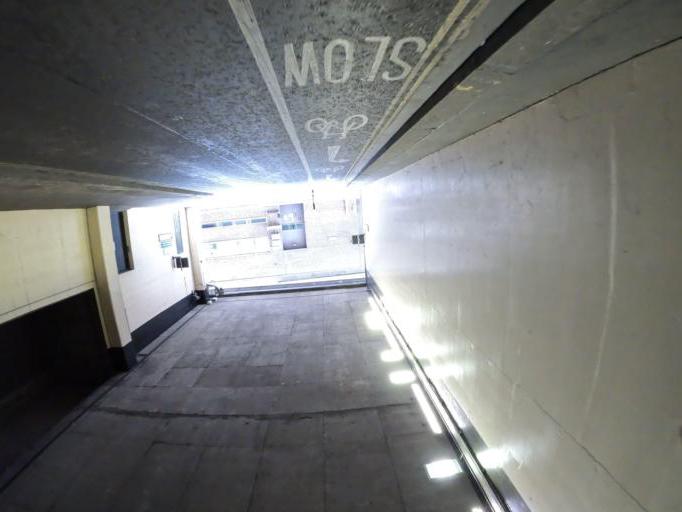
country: GB
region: England
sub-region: Greater London
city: Harringay
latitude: 51.5676
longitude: -0.0796
